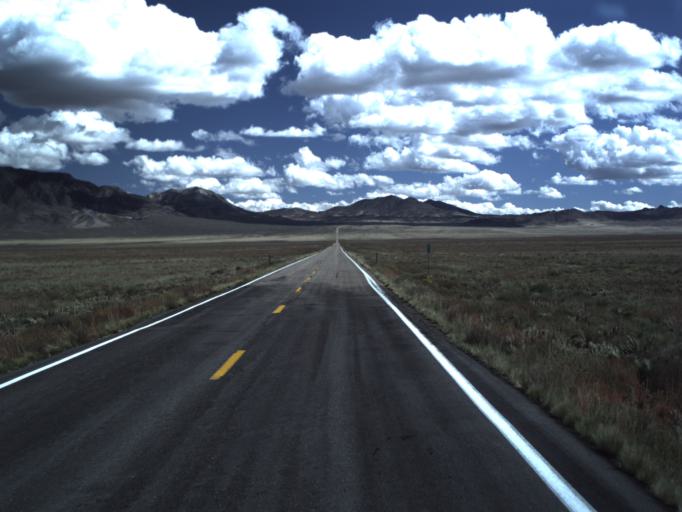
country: US
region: Utah
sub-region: Beaver County
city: Milford
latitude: 38.4712
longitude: -113.4092
